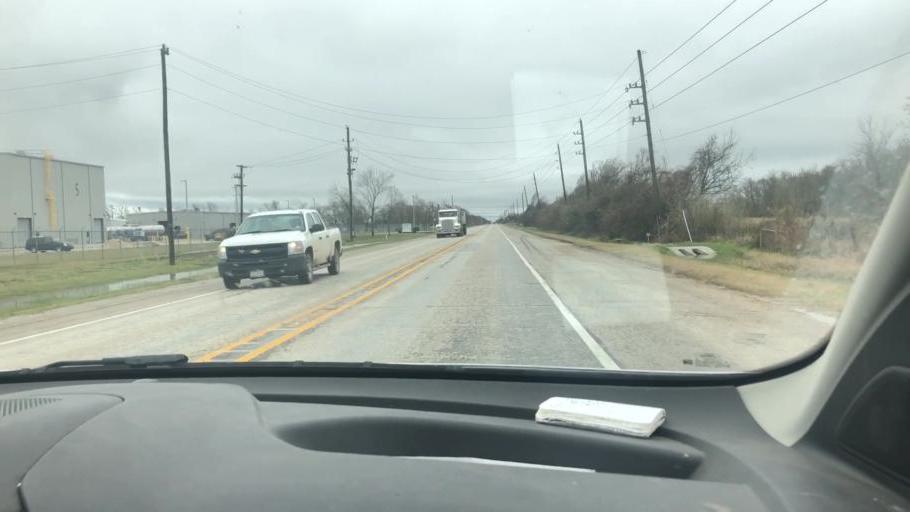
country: US
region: Texas
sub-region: Wharton County
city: Wharton
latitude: 29.2888
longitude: -96.0712
